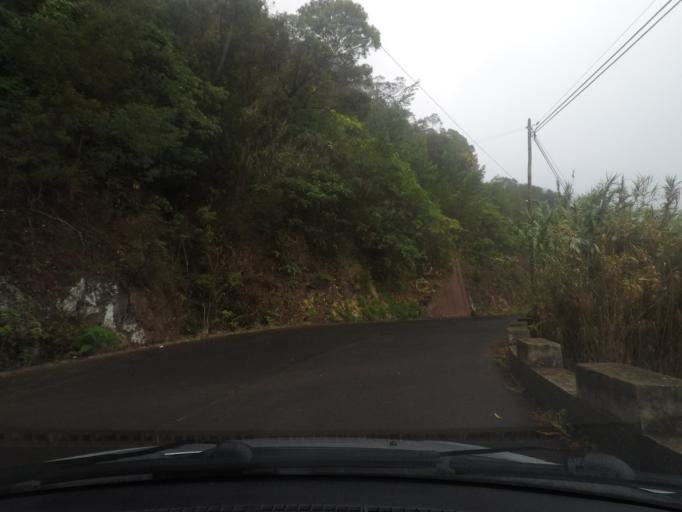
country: PT
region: Madeira
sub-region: Santana
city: Santana
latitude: 32.7809
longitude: -16.8621
